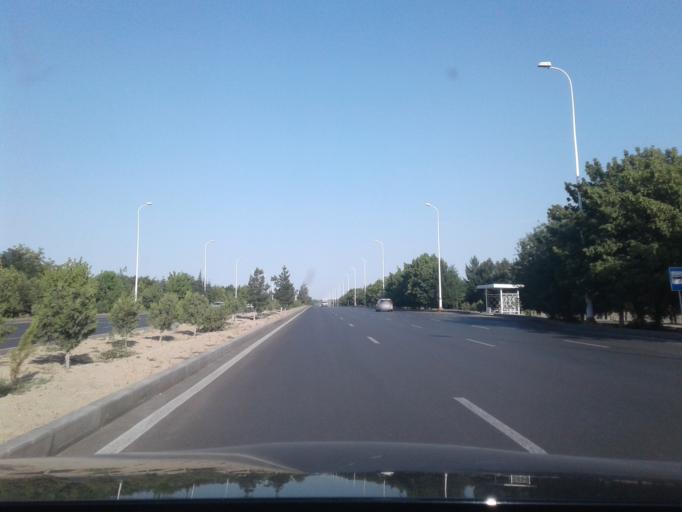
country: TM
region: Ahal
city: Abadan
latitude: 38.0144
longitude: 58.2665
